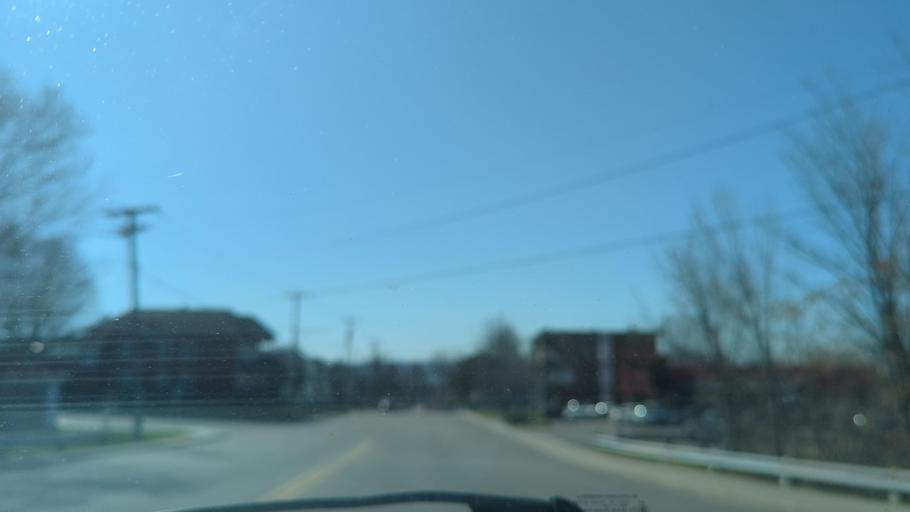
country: CA
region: Quebec
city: Quebec
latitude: 46.8554
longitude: -71.2164
